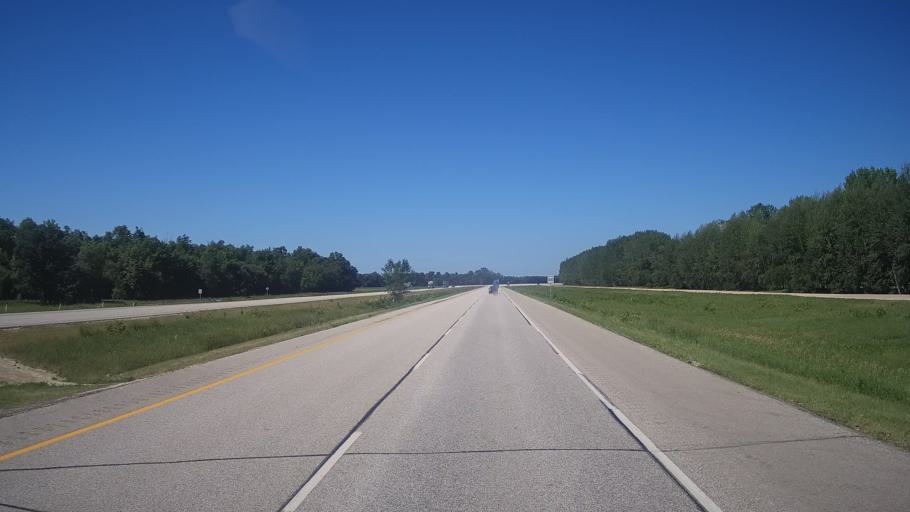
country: CA
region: Manitoba
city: Portage la Prairie
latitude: 49.9500
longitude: -98.2853
